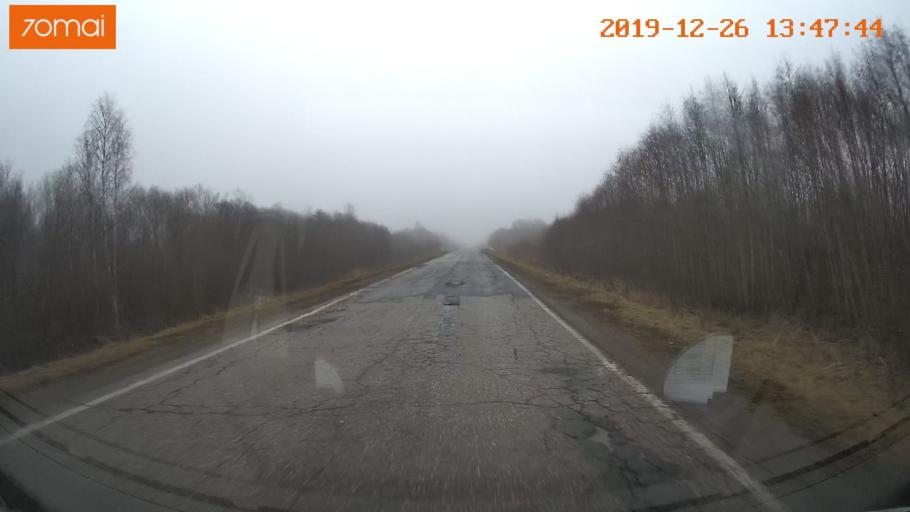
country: RU
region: Vologda
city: Sheksna
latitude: 58.6825
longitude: 38.5378
